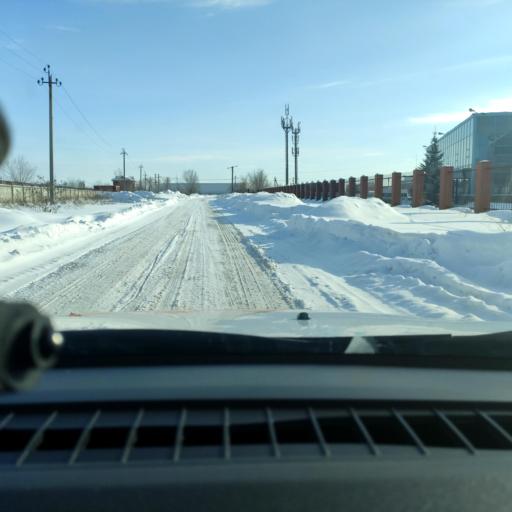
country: RU
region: Samara
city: Petra-Dubrava
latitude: 53.2636
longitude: 50.3489
